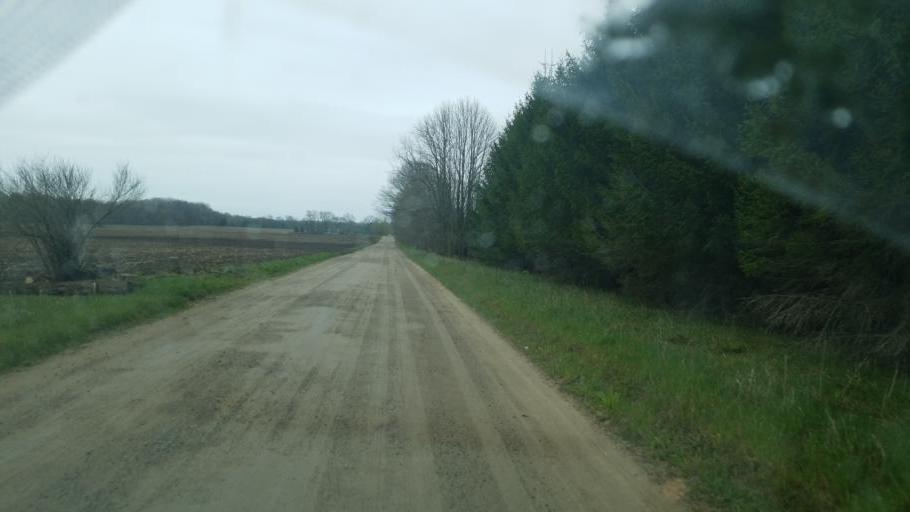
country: US
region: Michigan
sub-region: Montcalm County
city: Lakeview
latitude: 43.4893
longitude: -85.2799
